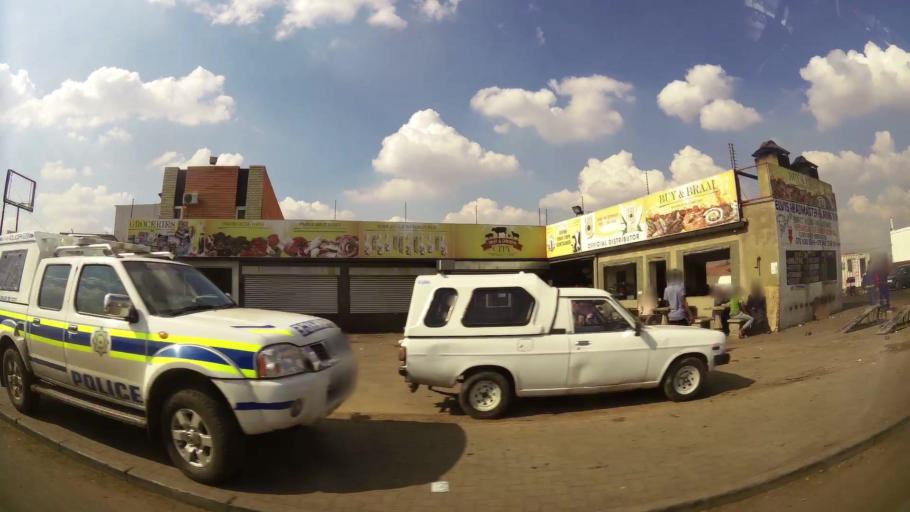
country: ZA
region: Gauteng
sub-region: Ekurhuleni Metropolitan Municipality
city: Germiston
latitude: -26.3303
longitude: 28.1440
